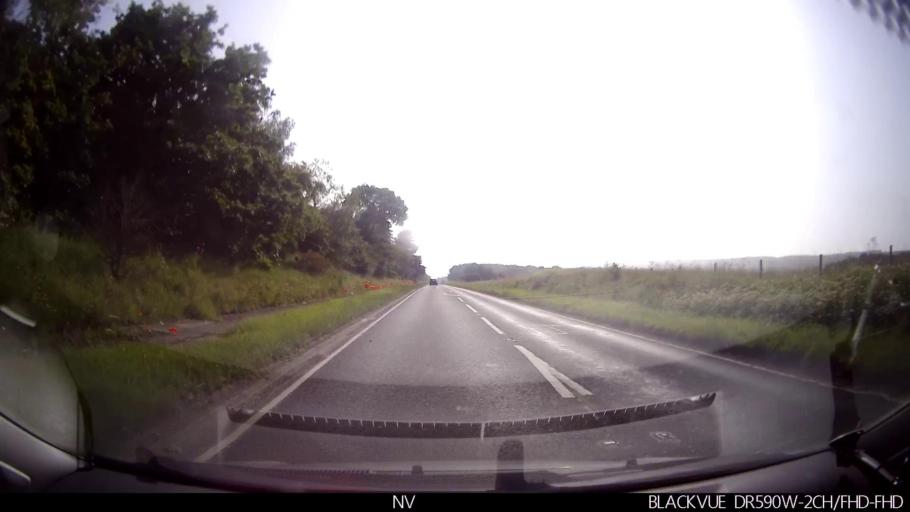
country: GB
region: England
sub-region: North Yorkshire
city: East Ayton
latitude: 54.1784
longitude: -0.5262
